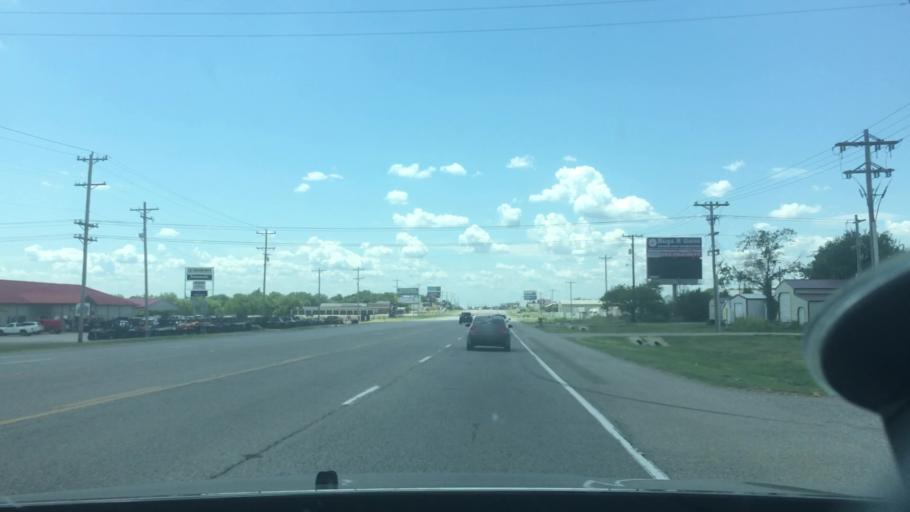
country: US
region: Oklahoma
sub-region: Bryan County
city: Calera
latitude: 33.9980
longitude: -96.4559
